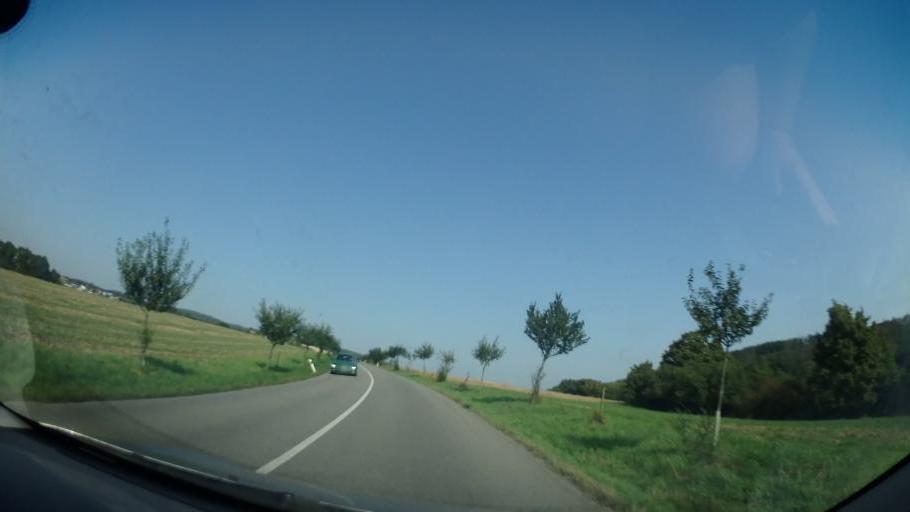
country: CZ
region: South Moravian
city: Kurim
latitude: 49.2462
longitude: 16.5297
